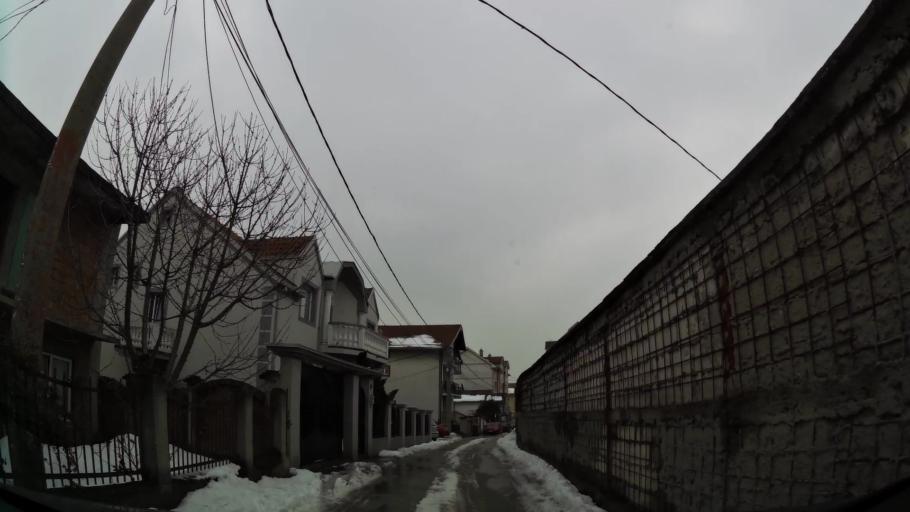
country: RS
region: Central Serbia
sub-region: Belgrade
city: Zvezdara
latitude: 44.7710
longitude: 20.5077
